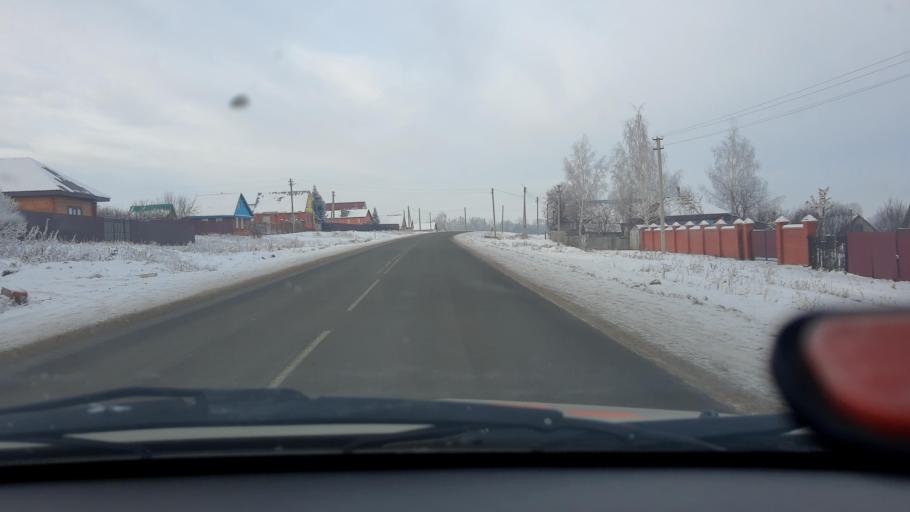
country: RU
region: Bashkortostan
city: Avdon
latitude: 54.3721
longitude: 55.8158
